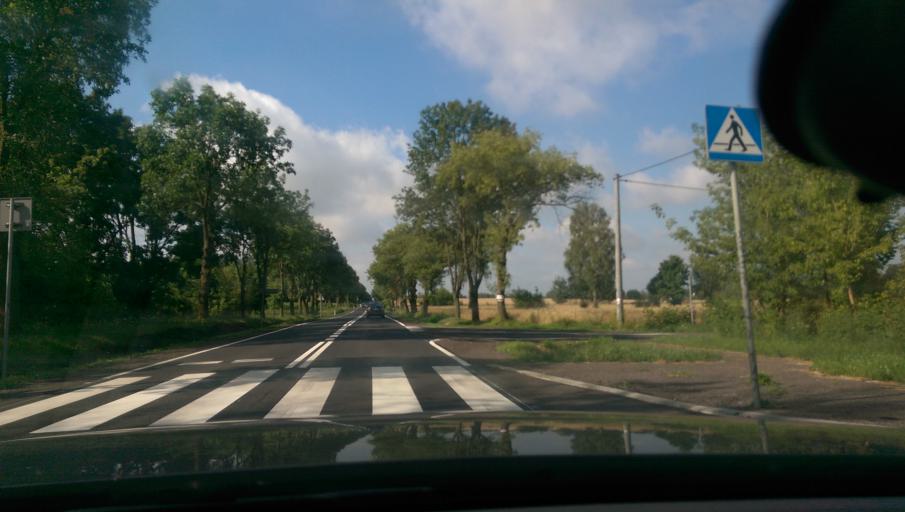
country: PL
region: Masovian Voivodeship
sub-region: Powiat ciechanowski
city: Ojrzen
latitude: 52.7460
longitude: 20.5280
